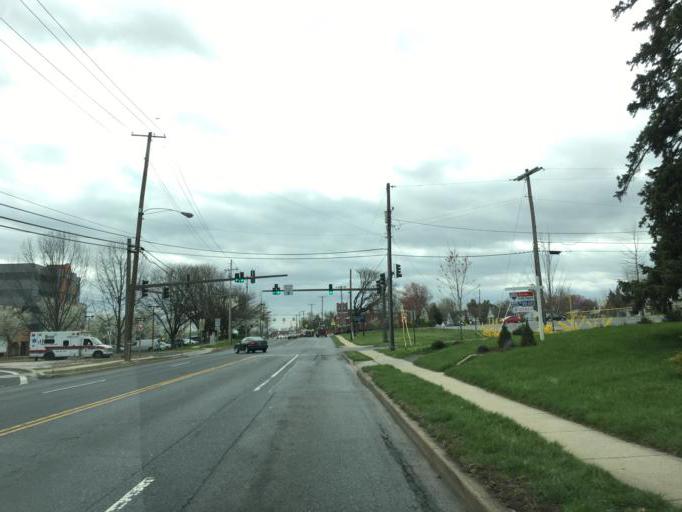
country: US
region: Maryland
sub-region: Frederick County
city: Frederick
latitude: 39.4284
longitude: -77.4194
